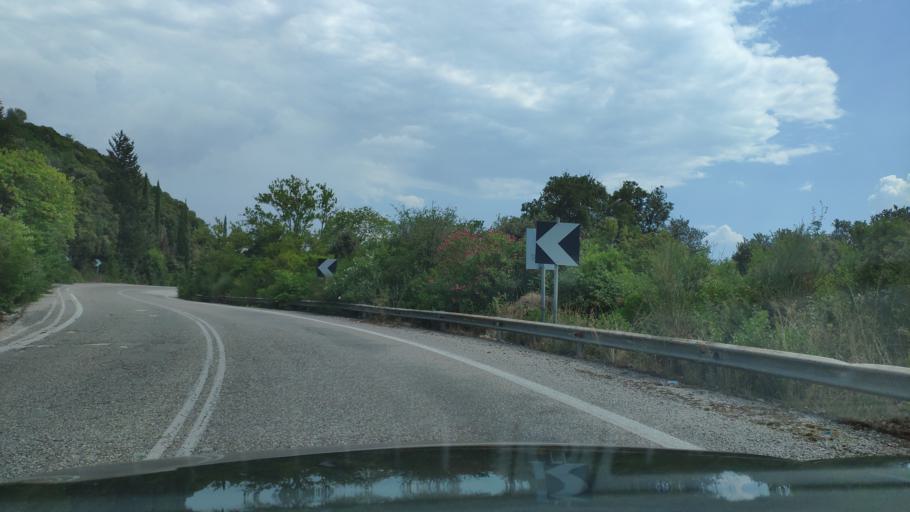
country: GR
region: West Greece
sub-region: Nomos Aitolias kai Akarnanias
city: Menidi
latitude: 39.0032
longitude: 21.1476
